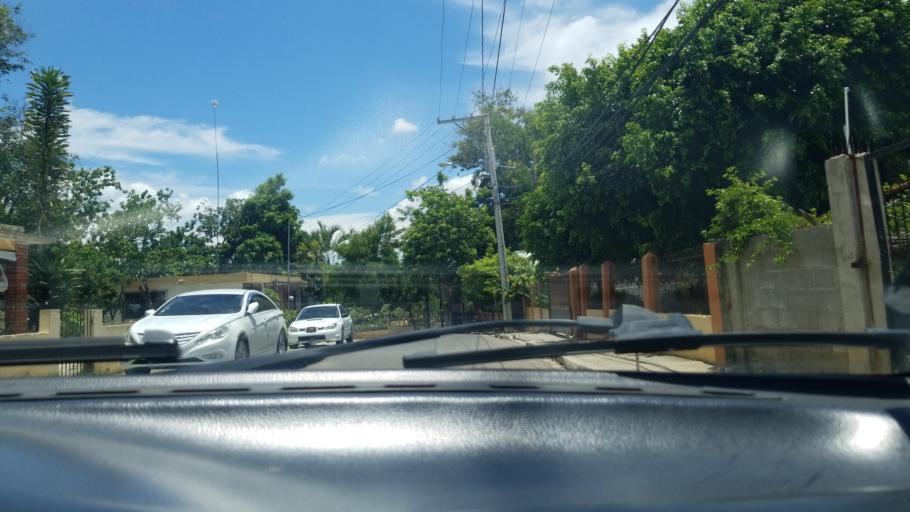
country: DO
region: Santiago
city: Santiago de los Caballeros
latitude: 19.4796
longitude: -70.6830
